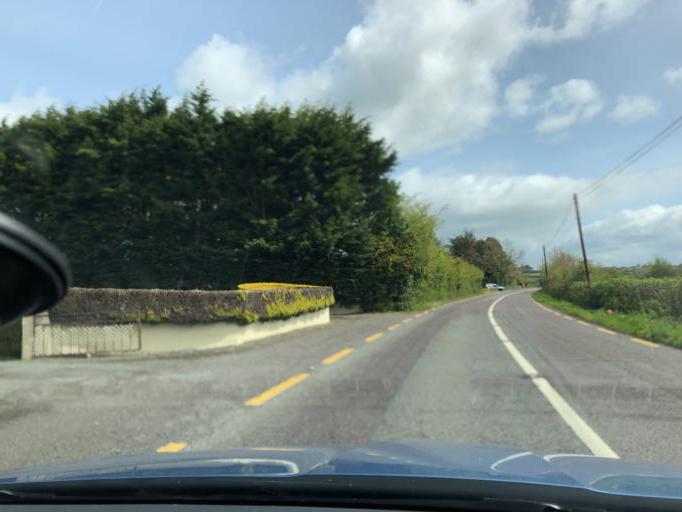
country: IE
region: Munster
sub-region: County Cork
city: Millstreet
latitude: 52.0903
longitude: -9.1460
